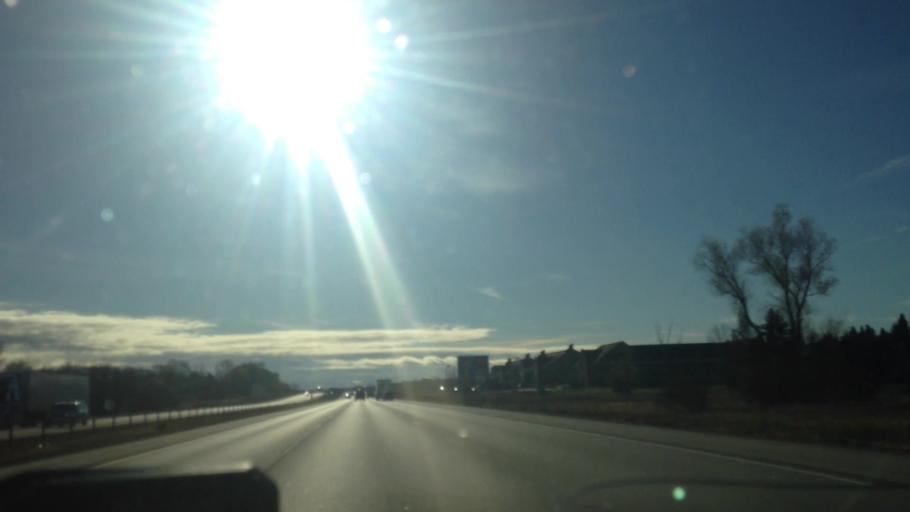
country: US
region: Wisconsin
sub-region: Waukesha County
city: Menomonee Falls
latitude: 43.1999
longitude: -88.1323
